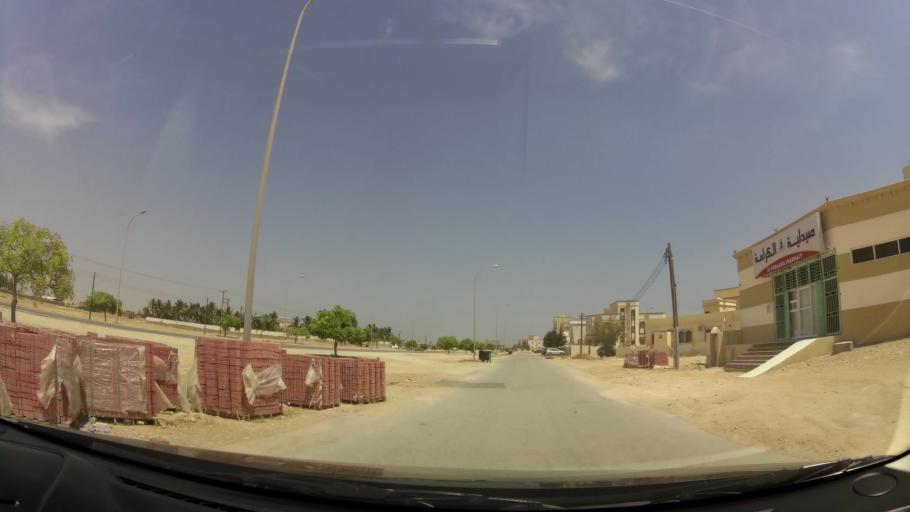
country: OM
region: Zufar
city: Salalah
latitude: 17.0633
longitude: 54.1605
